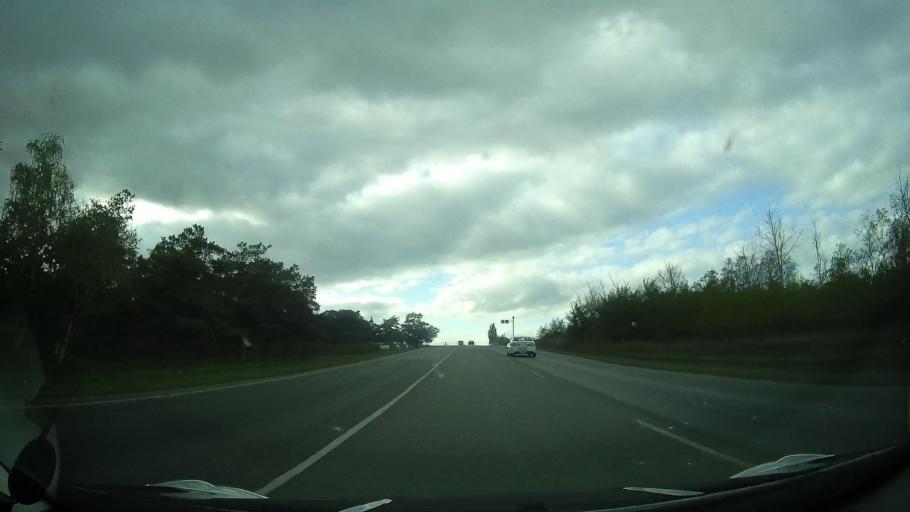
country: RU
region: Rostov
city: Kagal'nitskaya
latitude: 46.8900
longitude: 40.1349
